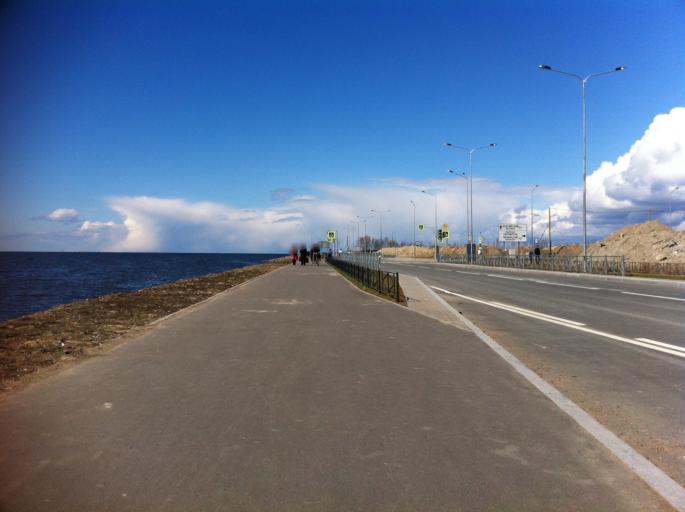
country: RU
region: St.-Petersburg
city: Sosnovaya Polyana
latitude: 59.8624
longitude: 30.1529
